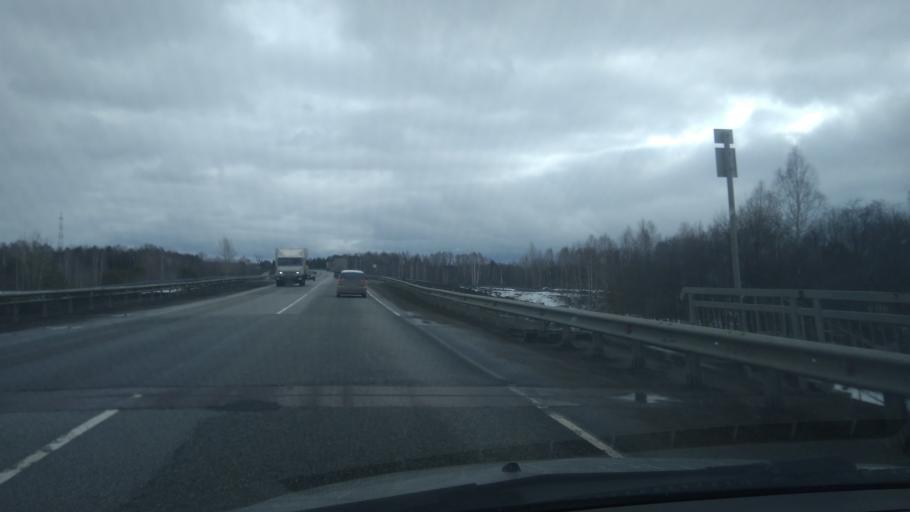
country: RU
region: Sverdlovsk
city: Ufimskiy
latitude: 56.7661
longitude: 58.1348
